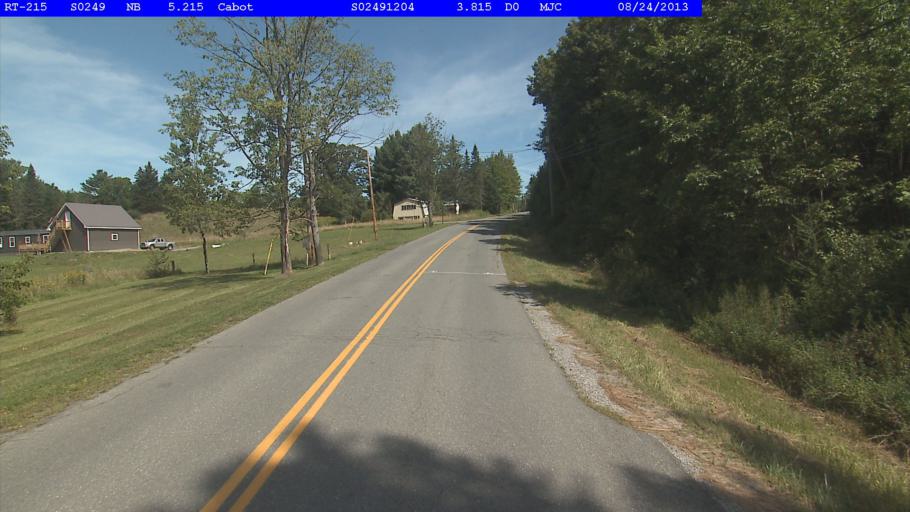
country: US
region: Vermont
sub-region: Caledonia County
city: Hardwick
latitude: 44.4111
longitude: -72.3038
